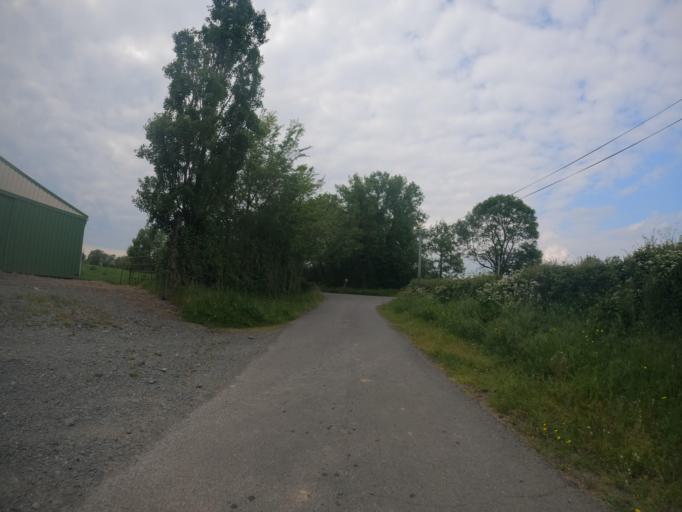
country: FR
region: Poitou-Charentes
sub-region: Departement des Deux-Sevres
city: Chiche
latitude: 46.8651
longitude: -0.3220
